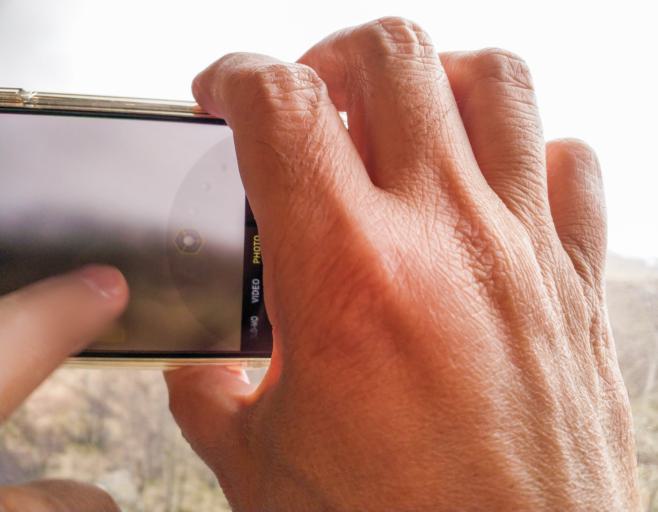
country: GB
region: Scotland
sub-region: Highland
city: Spean Bridge
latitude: 56.5552
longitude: -4.7284
